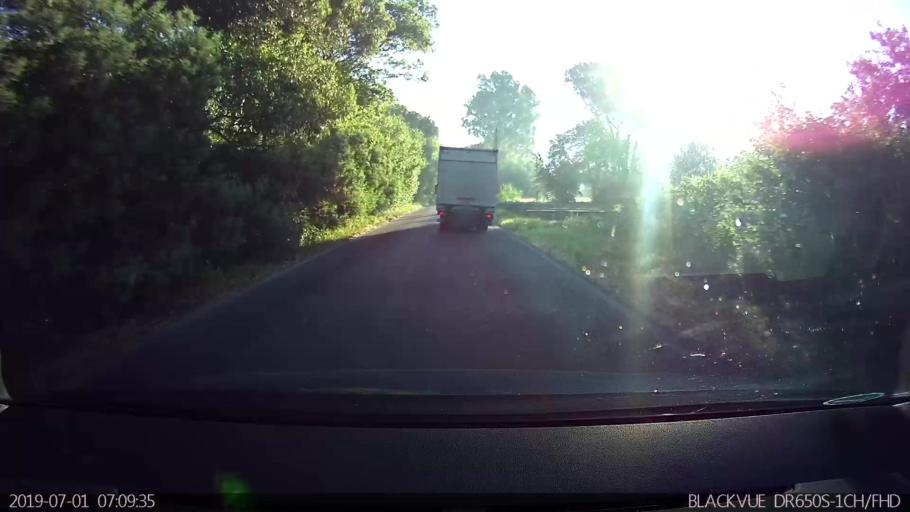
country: IT
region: Latium
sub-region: Provincia di Latina
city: Borgo Hermada
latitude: 41.3063
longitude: 13.1623
